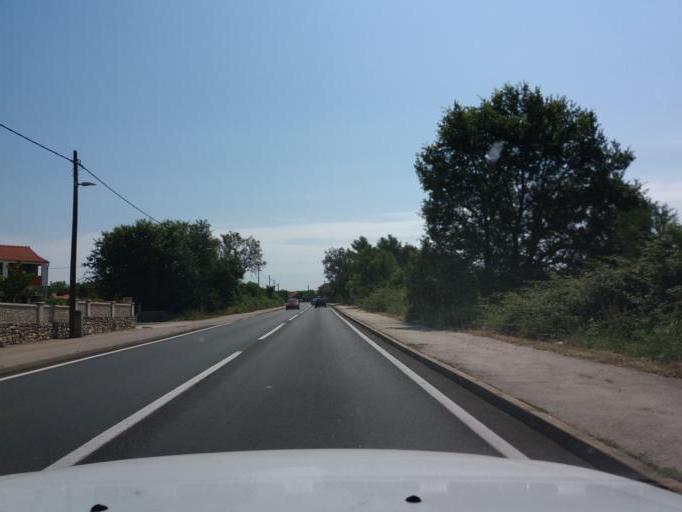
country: HR
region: Zadarska
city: Policnik
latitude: 44.1710
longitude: 15.3711
